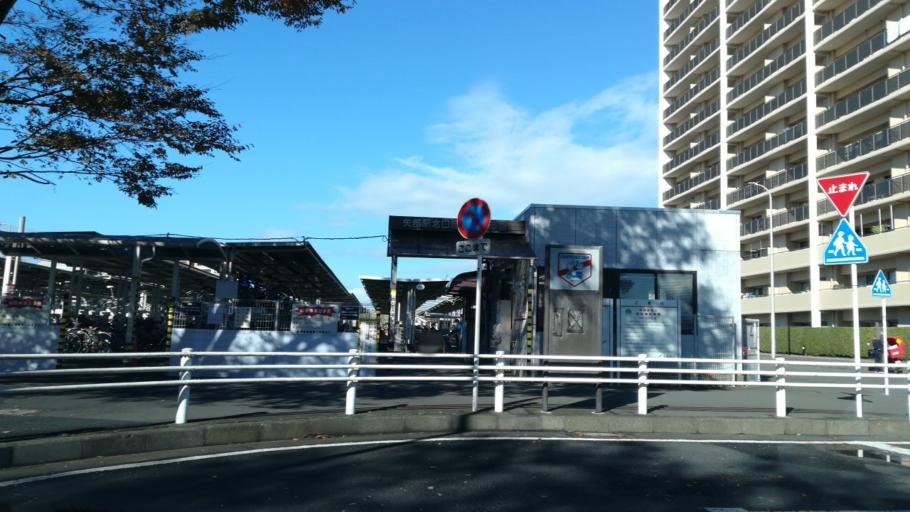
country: JP
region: Tokyo
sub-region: Machida-shi
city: Machida
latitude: 35.5734
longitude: 139.3870
